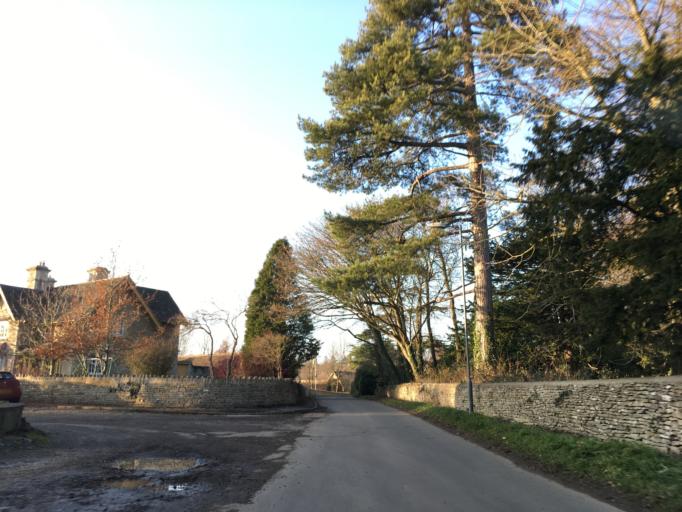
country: GB
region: England
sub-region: Wiltshire
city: Luckington
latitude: 51.5415
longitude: -2.2820
